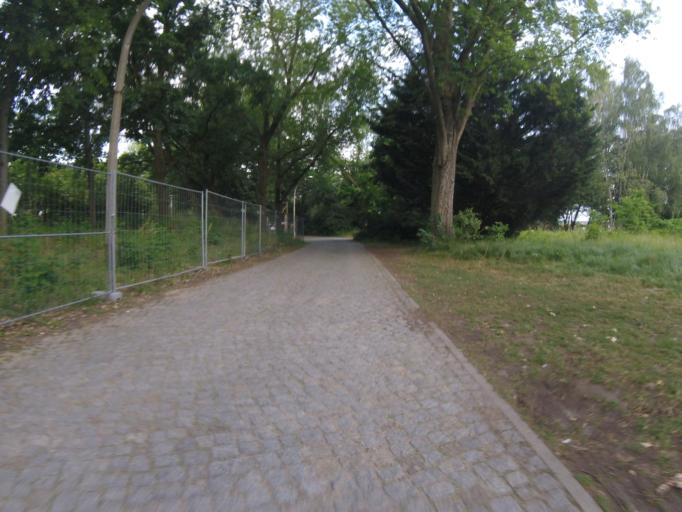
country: DE
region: Brandenburg
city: Konigs Wusterhausen
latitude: 52.3014
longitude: 13.6165
